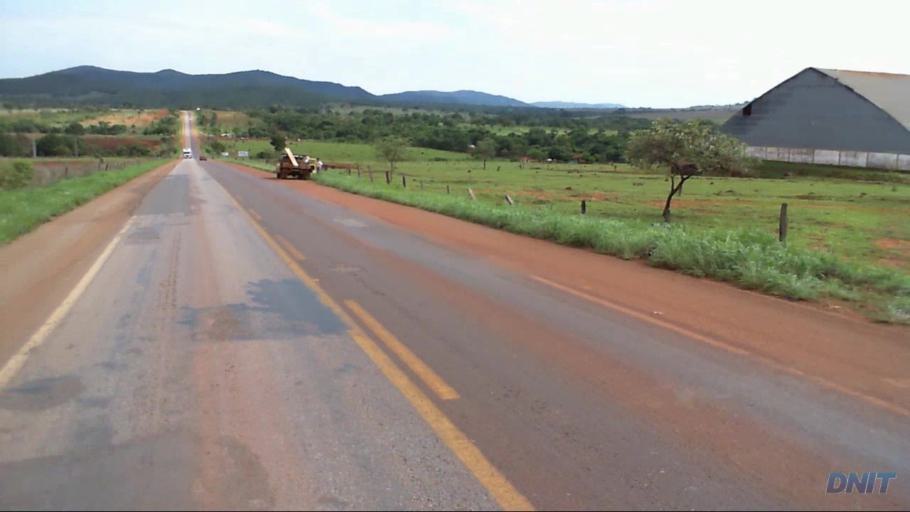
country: BR
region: Goias
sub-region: Barro Alto
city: Barro Alto
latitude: -14.9620
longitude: -48.9313
